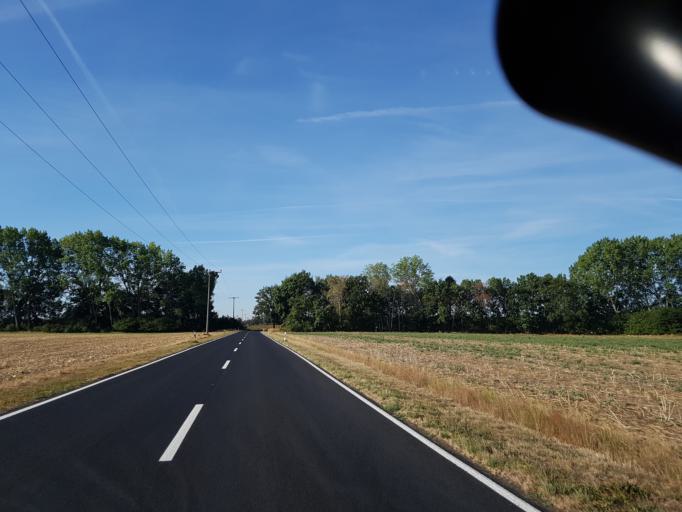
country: DE
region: Saxony
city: Nauwalde
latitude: 51.4521
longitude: 13.4599
